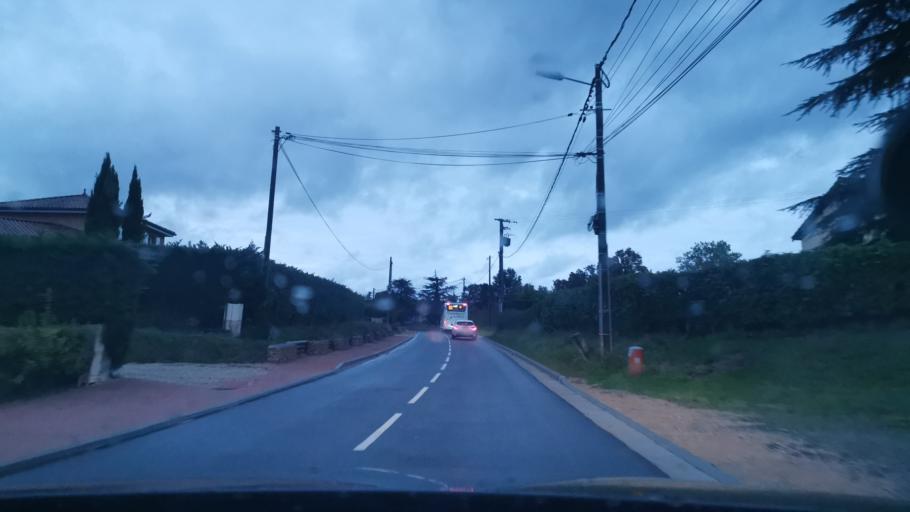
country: FR
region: Rhone-Alpes
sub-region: Departement de l'Ain
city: Crottet
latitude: 46.2697
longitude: 4.8981
